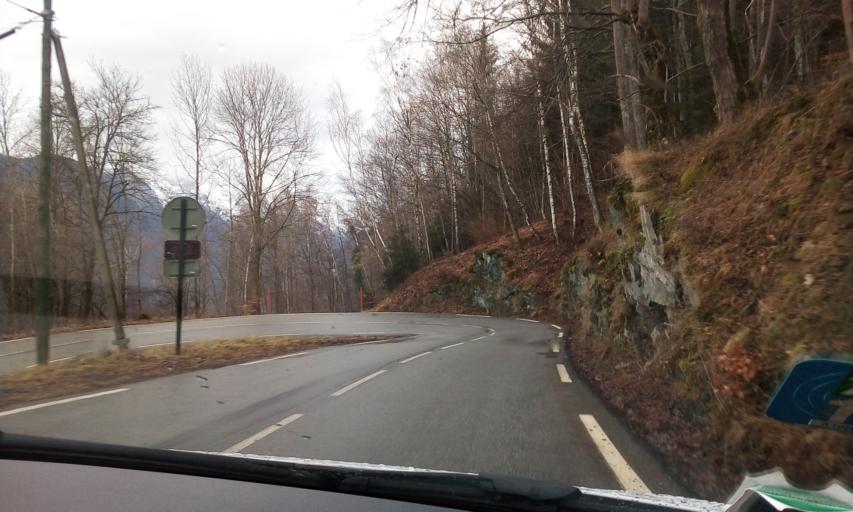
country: FR
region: Rhone-Alpes
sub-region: Departement de l'Isere
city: Vaulnaveys-le-Bas
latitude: 45.0482
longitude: 5.8456
